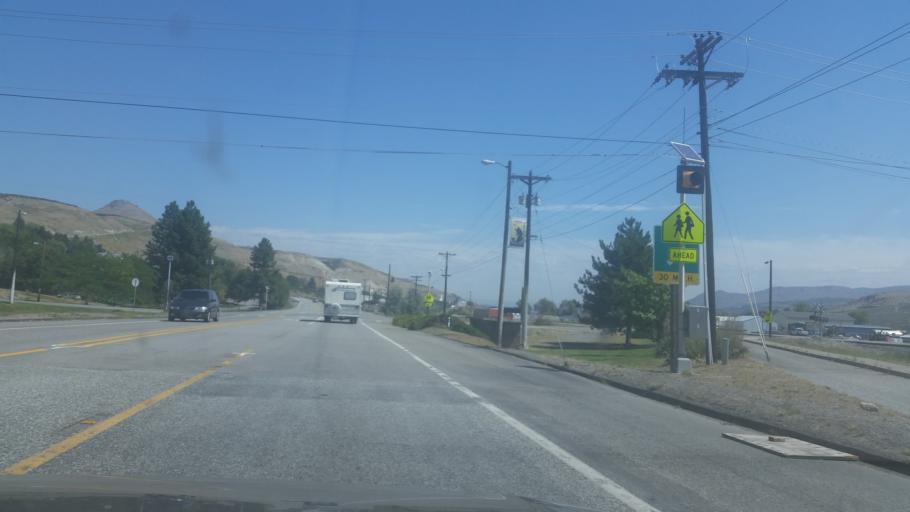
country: US
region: Washington
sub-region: Okanogan County
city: Brewster
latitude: 48.0545
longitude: -119.9006
